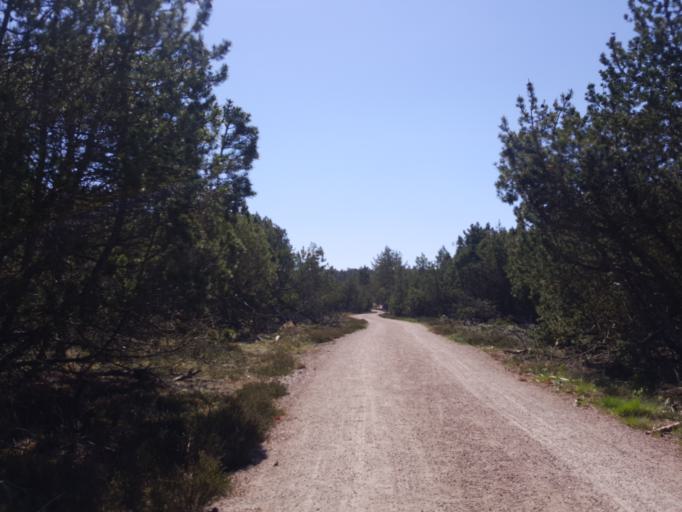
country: SE
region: Halland
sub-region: Laholms Kommun
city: Mellbystrand
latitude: 56.5255
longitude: 12.9588
